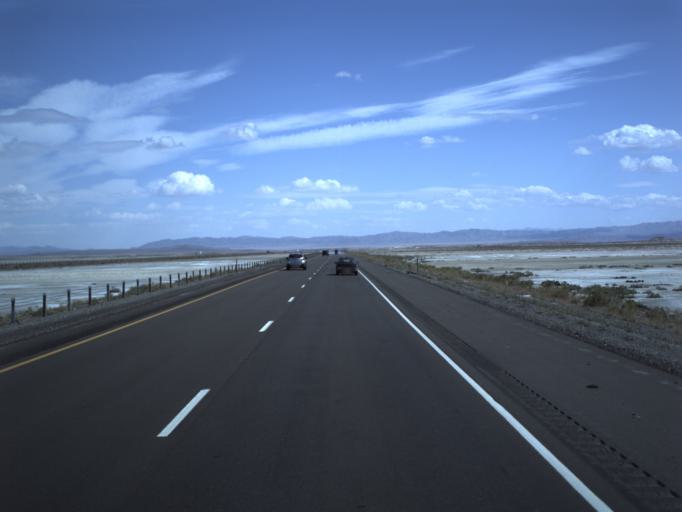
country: US
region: Utah
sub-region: Tooele County
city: Wendover
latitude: 40.7275
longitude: -113.3284
